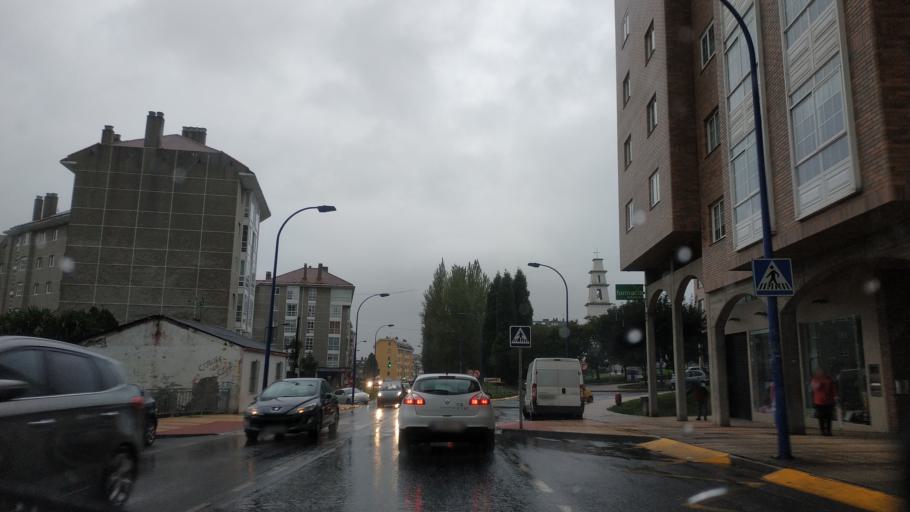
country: ES
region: Galicia
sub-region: Provincia da Coruna
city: Culleredo
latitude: 43.3187
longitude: -8.3844
